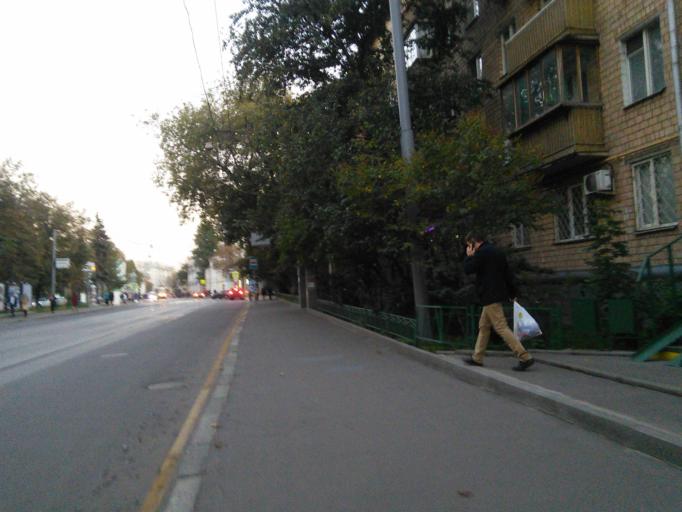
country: RU
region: Moscow
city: Zamoskvorech'ye
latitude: 55.7374
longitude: 37.6312
